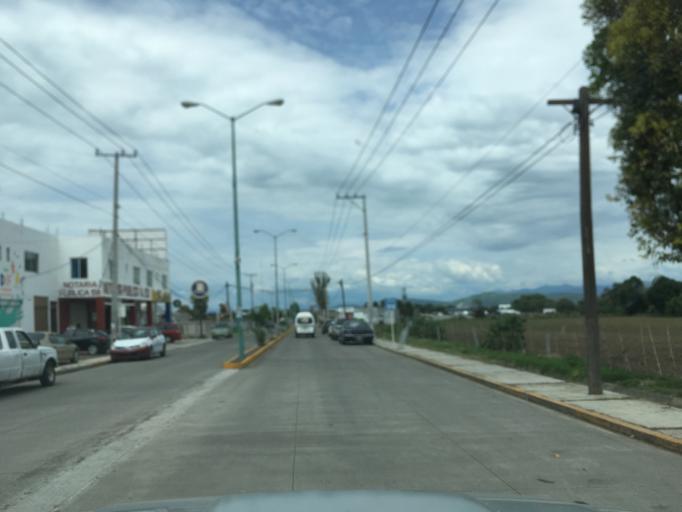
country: MX
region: Michoacan
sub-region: Tarimbaro
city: Meson Nuevo (Canada de la Magdalena)
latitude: 19.7967
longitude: -101.1667
